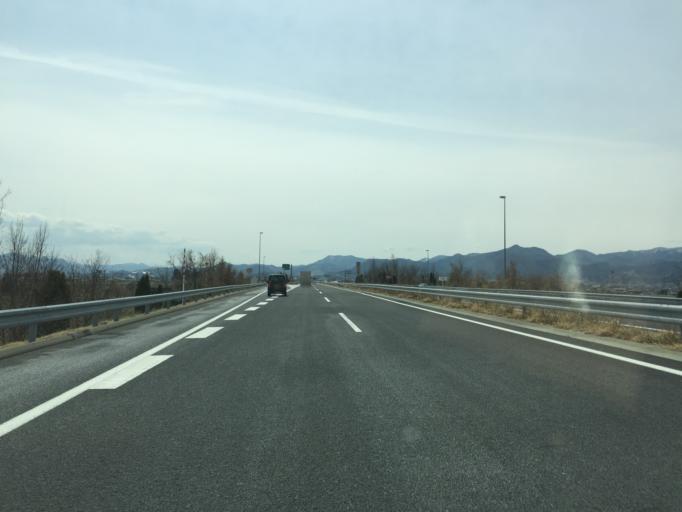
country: JP
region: Yamagata
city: Yamagata-shi
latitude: 38.2733
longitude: 140.2944
